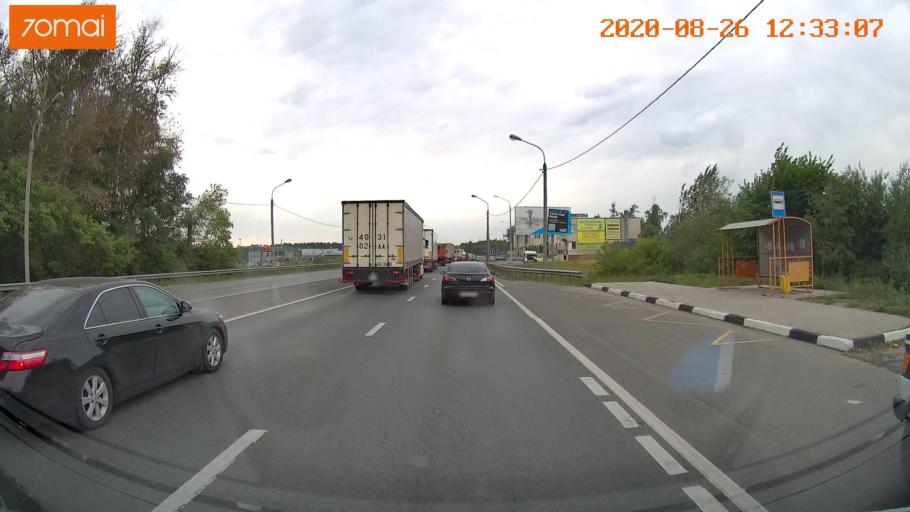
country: RU
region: Rjazan
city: Ryazan'
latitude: 54.5806
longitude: 39.7800
